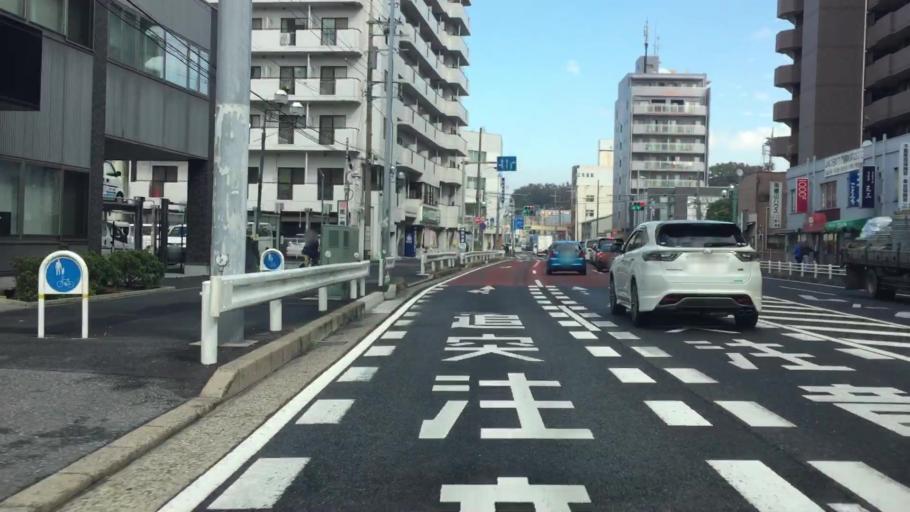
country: JP
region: Chiba
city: Matsudo
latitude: 35.7994
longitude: 139.9121
